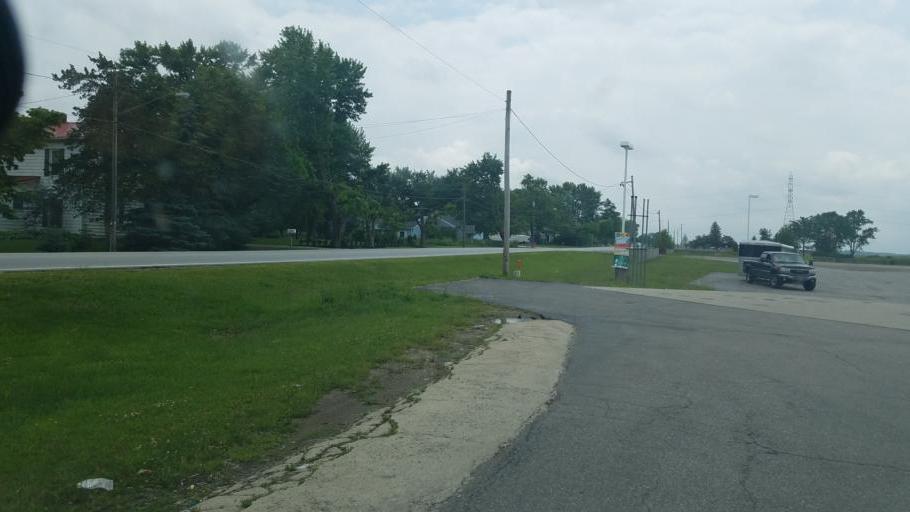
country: US
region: Ohio
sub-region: Union County
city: Richwood
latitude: 40.3449
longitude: -83.3065
